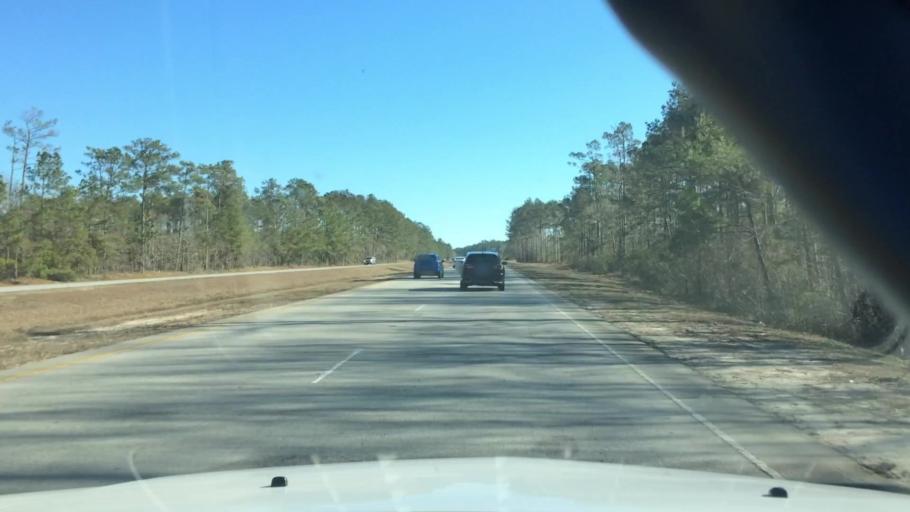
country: US
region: North Carolina
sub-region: Brunswick County
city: Bolivia
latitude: 34.0644
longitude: -78.1923
